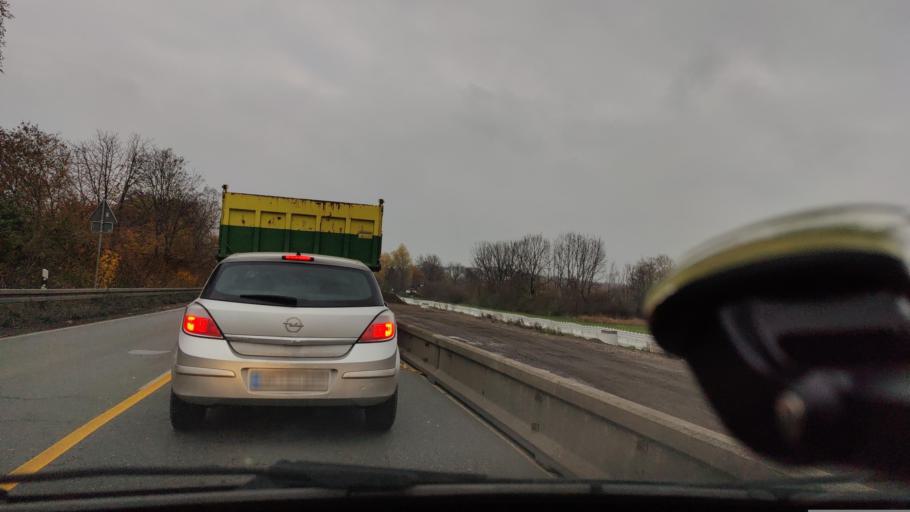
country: DE
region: North Rhine-Westphalia
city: Lunen
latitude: 51.5993
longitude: 7.4875
